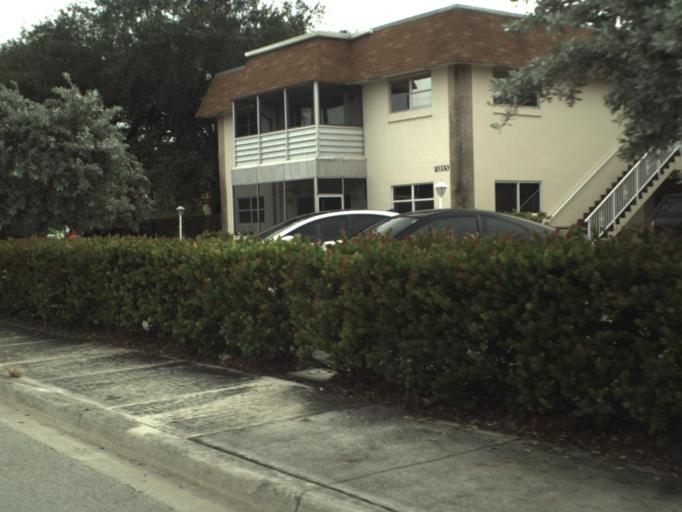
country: US
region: Florida
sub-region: Palm Beach County
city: North Palm Beach
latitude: 26.8283
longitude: -80.1054
